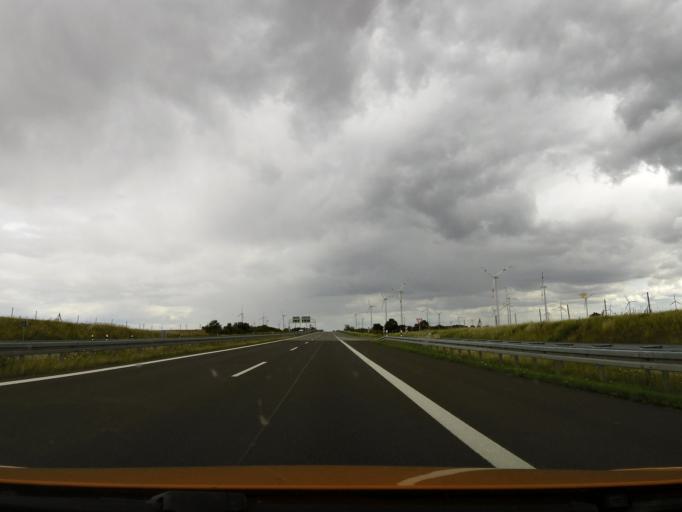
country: DE
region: Brandenburg
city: Gramzow
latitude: 53.2477
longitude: 14.0152
